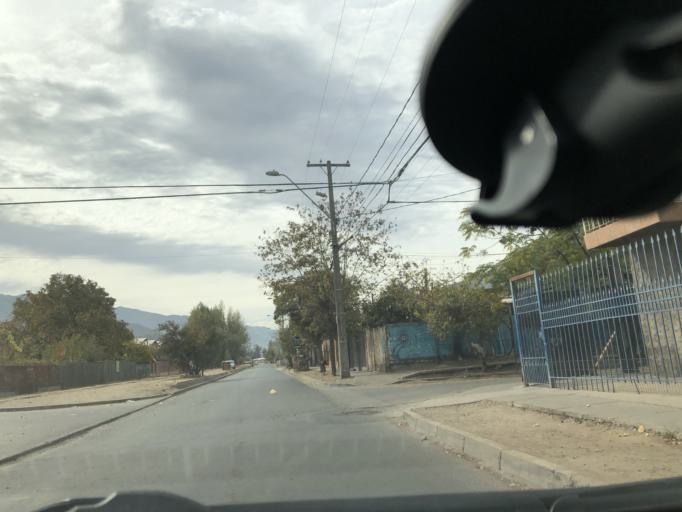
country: CL
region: Santiago Metropolitan
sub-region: Provincia de Cordillera
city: Puente Alto
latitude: -33.6092
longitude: -70.5204
